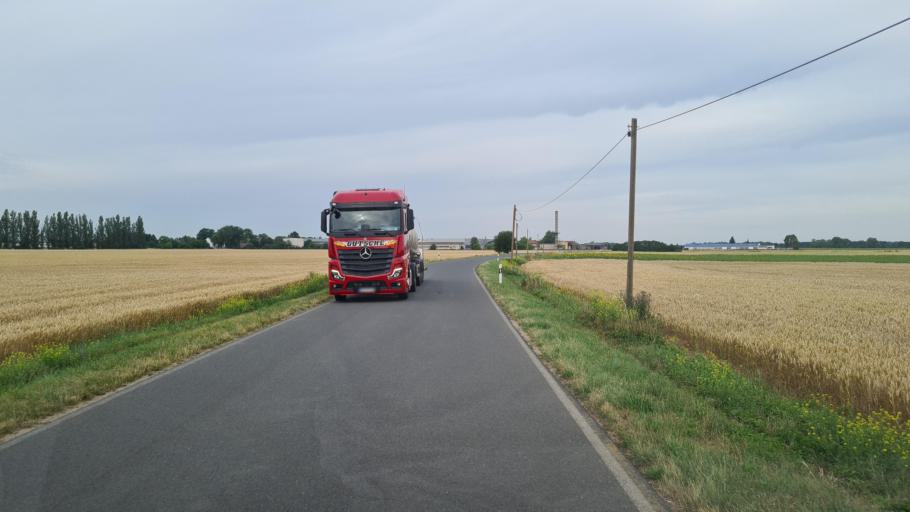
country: DE
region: Saxony-Anhalt
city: Jessen
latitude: 51.7559
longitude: 12.9611
